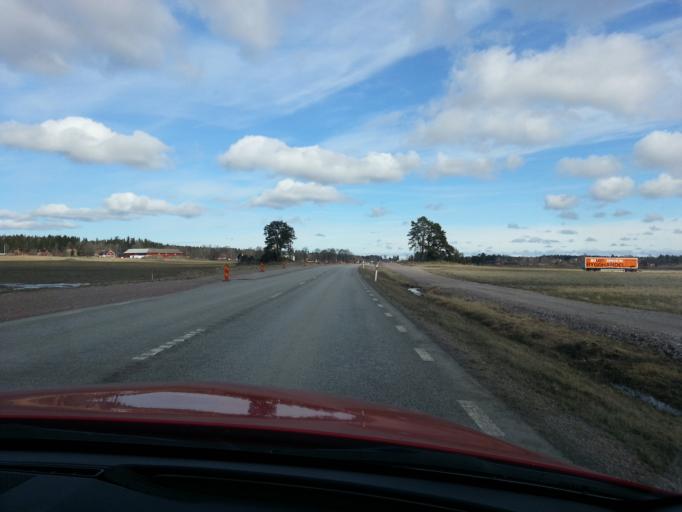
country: SE
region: Uppsala
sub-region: Osthammars Kommun
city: Gimo
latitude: 60.0544
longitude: 18.0592
